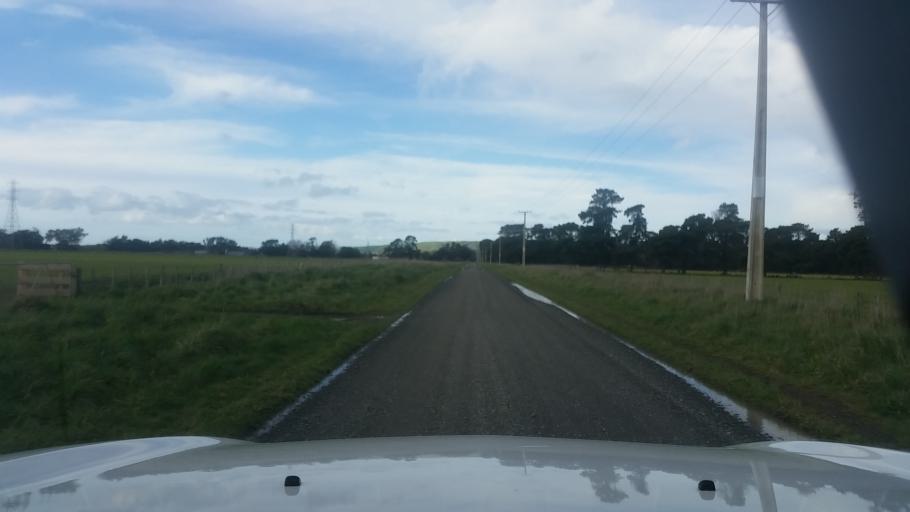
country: NZ
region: Wellington
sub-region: Masterton District
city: Masterton
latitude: -41.1190
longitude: 175.4240
